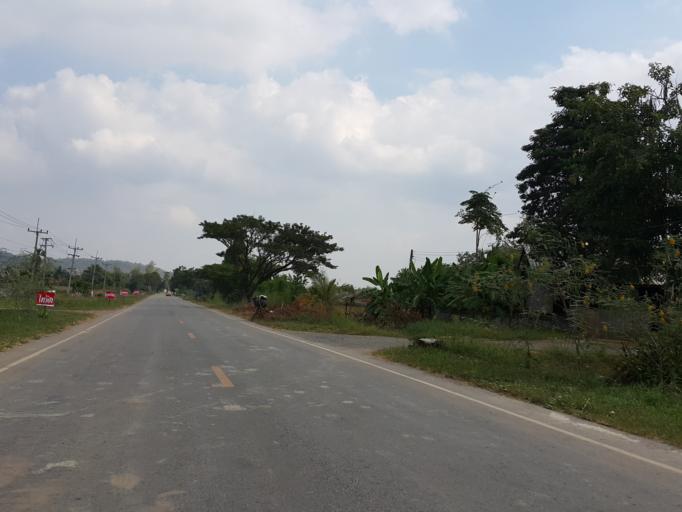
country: TH
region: Sukhothai
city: Thung Saliam
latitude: 17.3292
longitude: 99.5155
